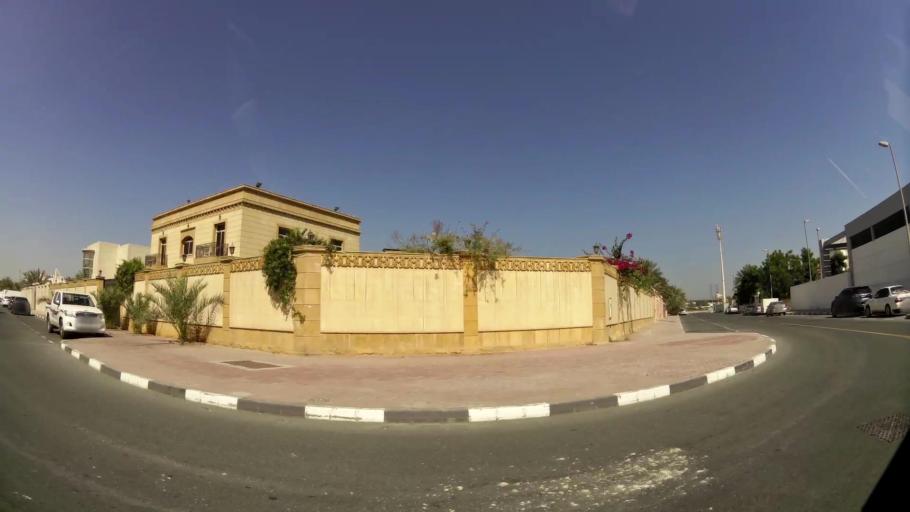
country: AE
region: Ash Shariqah
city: Sharjah
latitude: 25.2475
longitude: 55.2823
